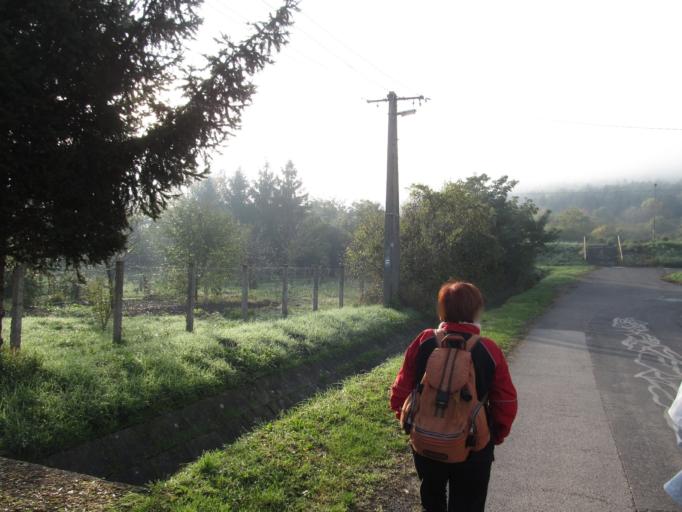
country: HU
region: Nograd
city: Matraverebely
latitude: 47.9691
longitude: 19.7809
